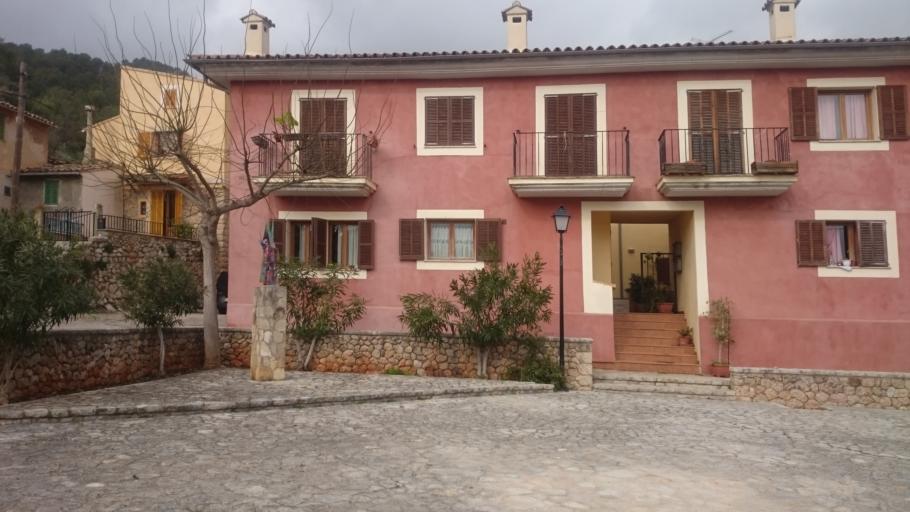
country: ES
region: Balearic Islands
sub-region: Illes Balears
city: Alaro
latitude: 39.7084
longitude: 2.7830
